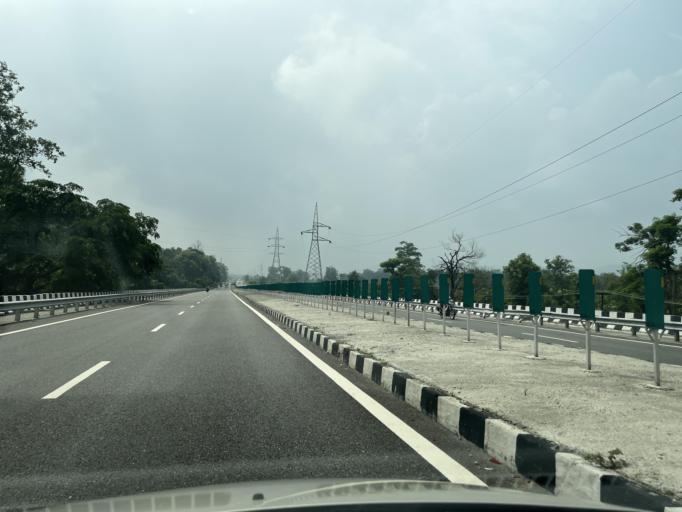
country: IN
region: Uttarakhand
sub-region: Dehradun
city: Raiwala
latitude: 30.0959
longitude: 78.1812
